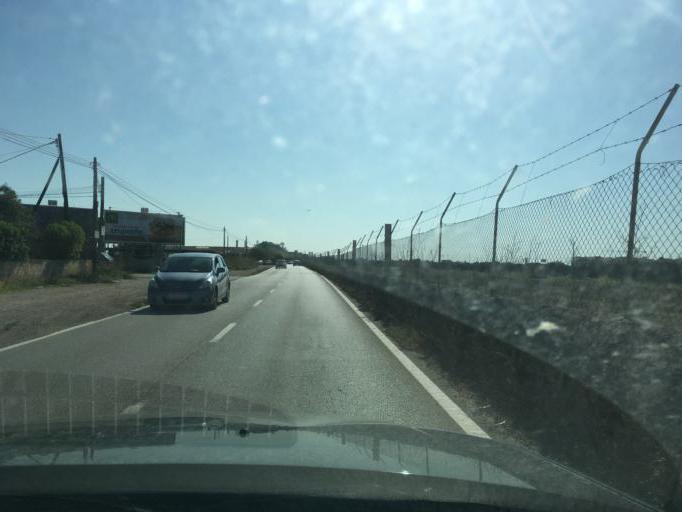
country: ES
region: Balearic Islands
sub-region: Illes Balears
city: Palma
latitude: 39.5794
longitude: 2.6840
